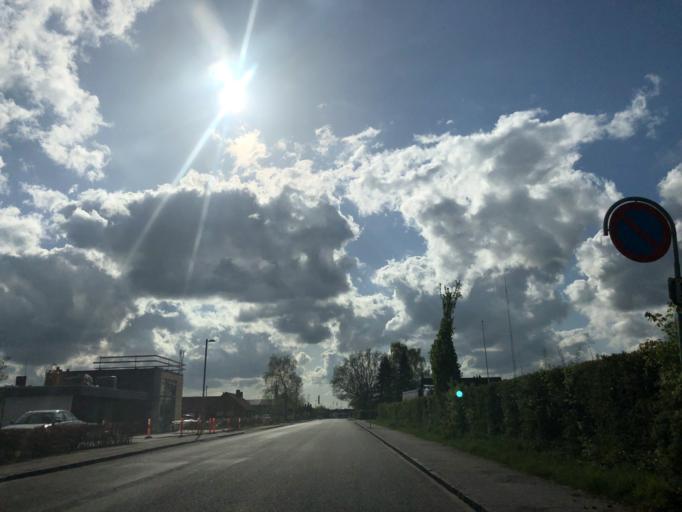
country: DK
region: Zealand
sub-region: Ringsted Kommune
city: Ringsted
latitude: 55.4333
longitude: 11.8001
